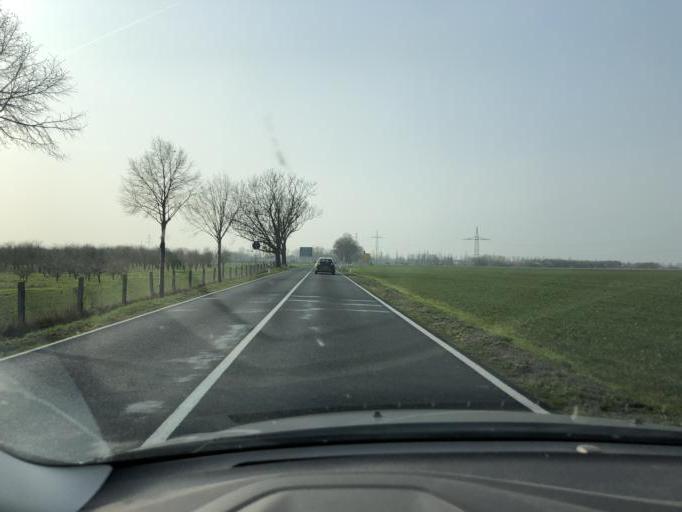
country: DE
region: Saxony-Anhalt
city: Brehna
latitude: 51.5497
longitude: 12.2373
